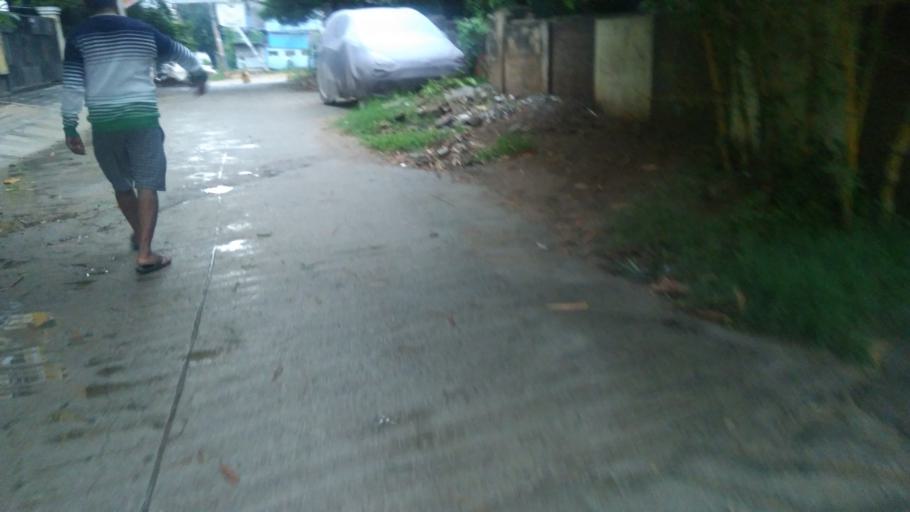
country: IN
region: Telangana
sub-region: Rangareddi
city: Secunderabad
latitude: 17.4798
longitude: 78.5374
